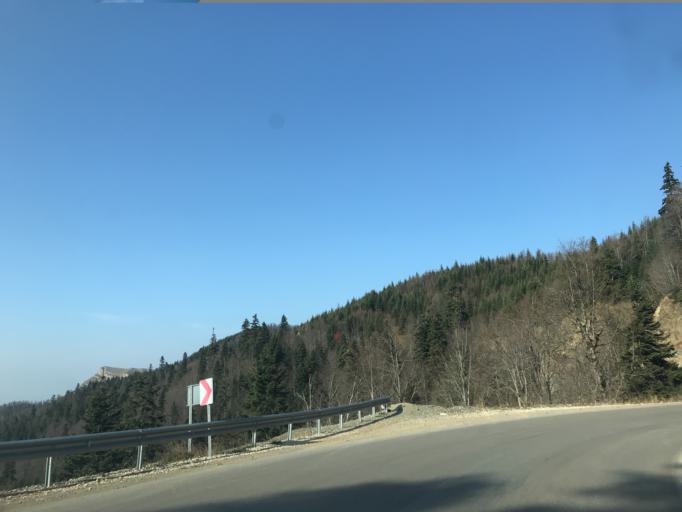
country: TR
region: Bolu
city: Bolu
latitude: 40.8845
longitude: 31.6822
